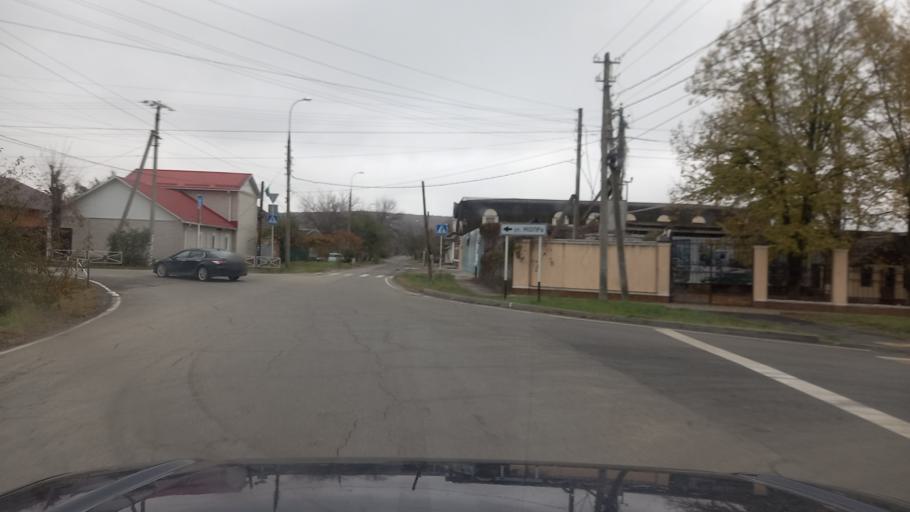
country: RU
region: Adygeya
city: Maykop
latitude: 44.5996
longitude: 40.0729
